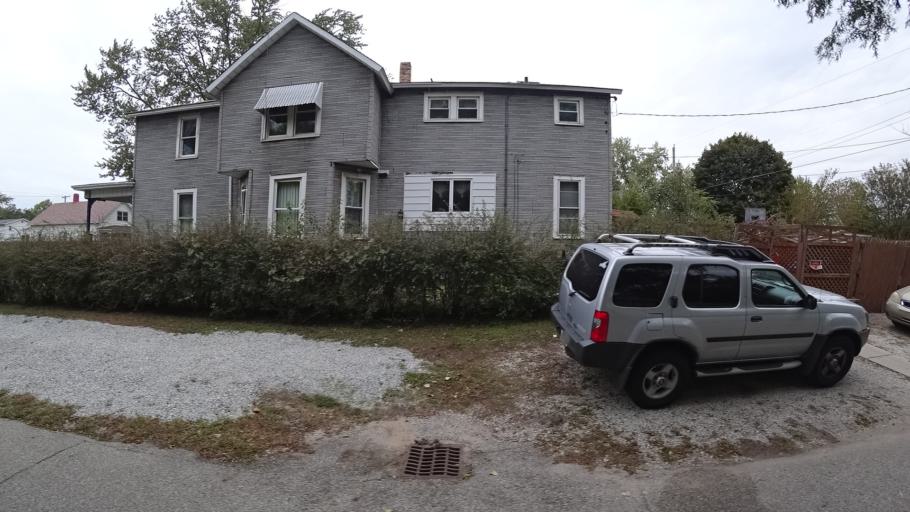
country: US
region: Indiana
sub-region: LaPorte County
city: Michigan City
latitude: 41.7026
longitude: -86.9015
